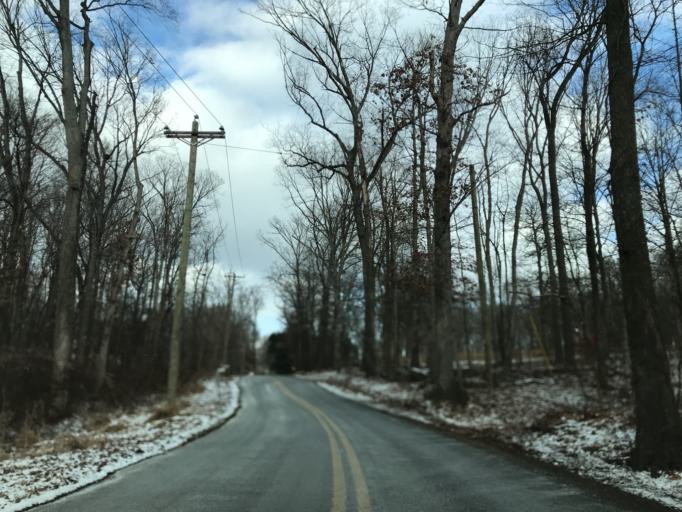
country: US
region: Maryland
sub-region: Harford County
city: Jarrettsville
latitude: 39.6580
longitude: -76.4054
